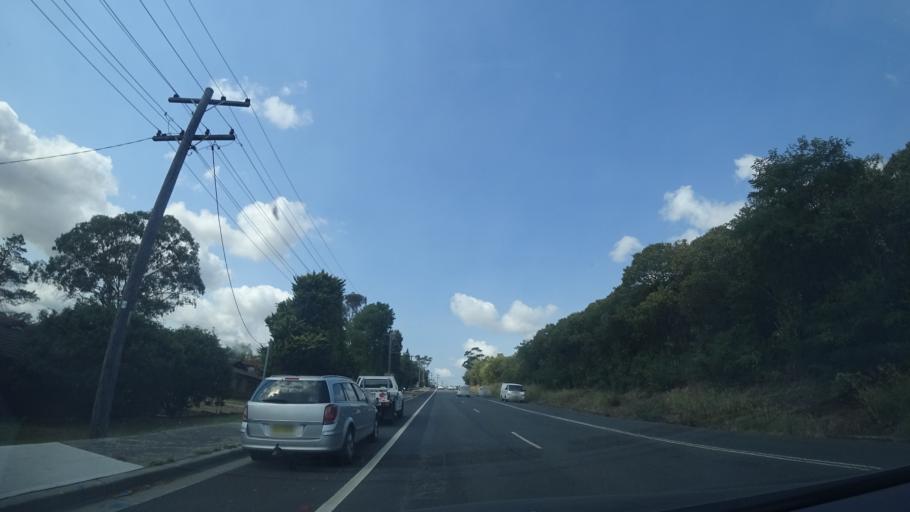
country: AU
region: New South Wales
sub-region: Wollondilly
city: Picton
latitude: -34.1807
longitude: 150.6083
